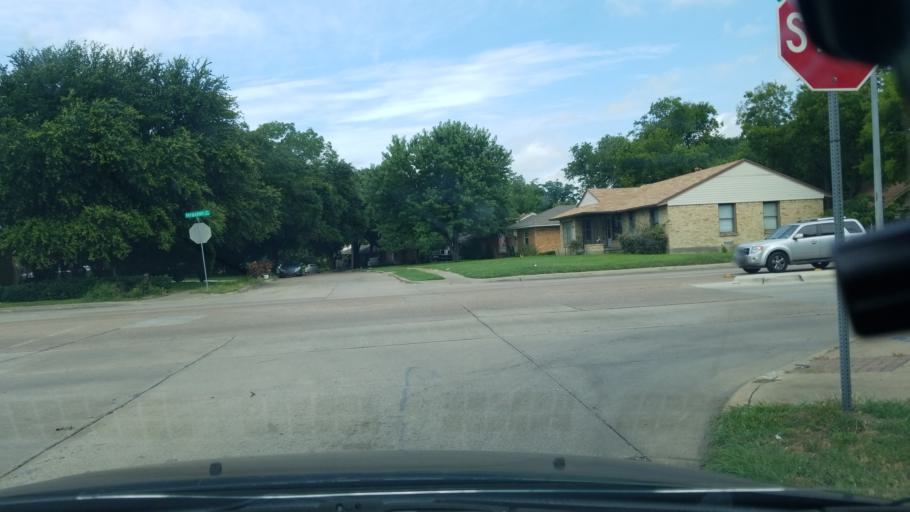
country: US
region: Texas
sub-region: Dallas County
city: Garland
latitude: 32.8280
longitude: -96.6759
